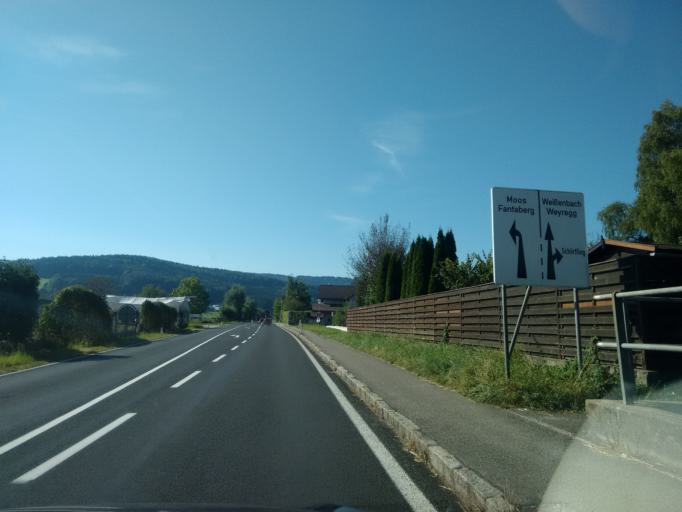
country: AT
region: Upper Austria
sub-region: Politischer Bezirk Vocklabruck
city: Lenzing
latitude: 47.9485
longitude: 13.6114
